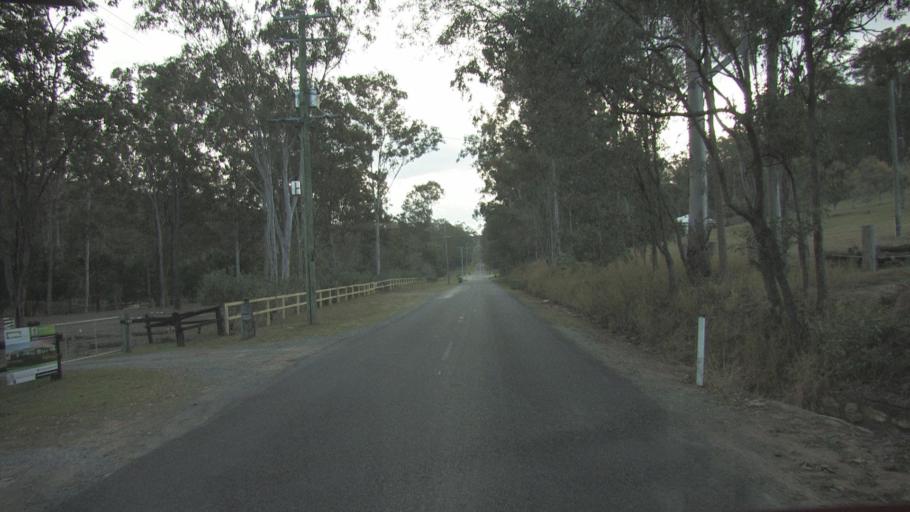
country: AU
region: Queensland
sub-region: Logan
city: Cedar Vale
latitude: -27.8392
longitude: 153.1005
